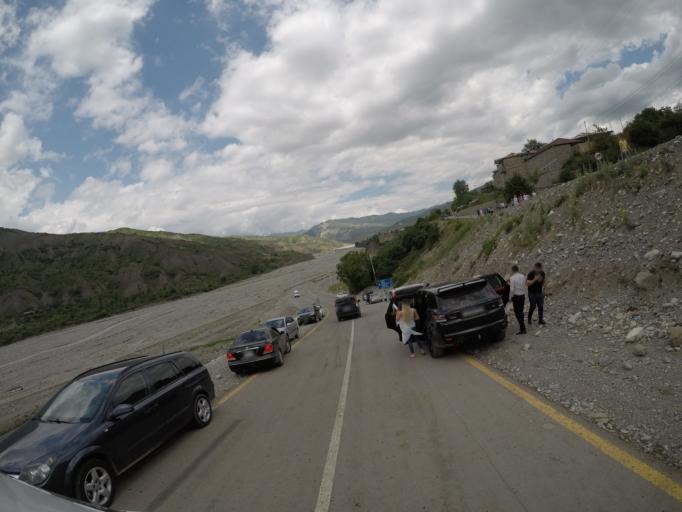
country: AZ
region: Ismayilli
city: Basqal
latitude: 40.8446
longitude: 48.3779
